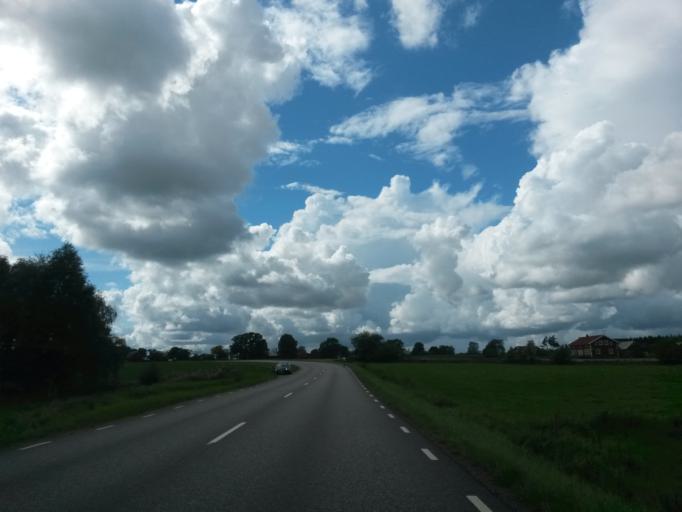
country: SE
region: Vaestra Goetaland
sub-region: Herrljunga Kommun
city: Herrljunga
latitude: 57.9955
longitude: 12.9452
